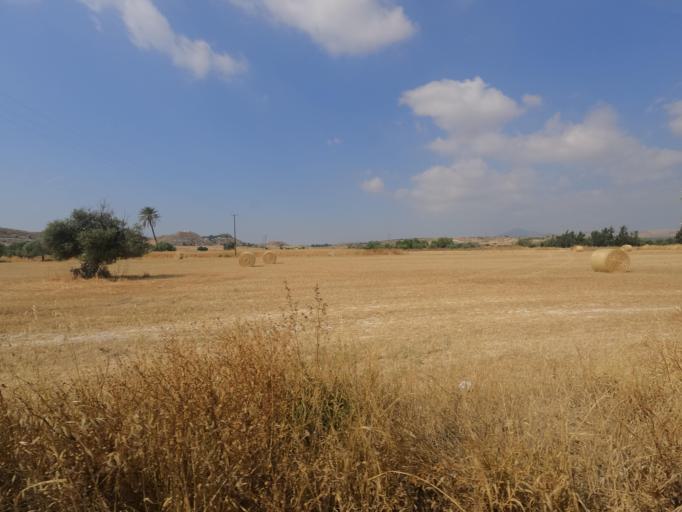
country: CY
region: Larnaka
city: Aradippou
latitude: 34.9237
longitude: 33.5408
